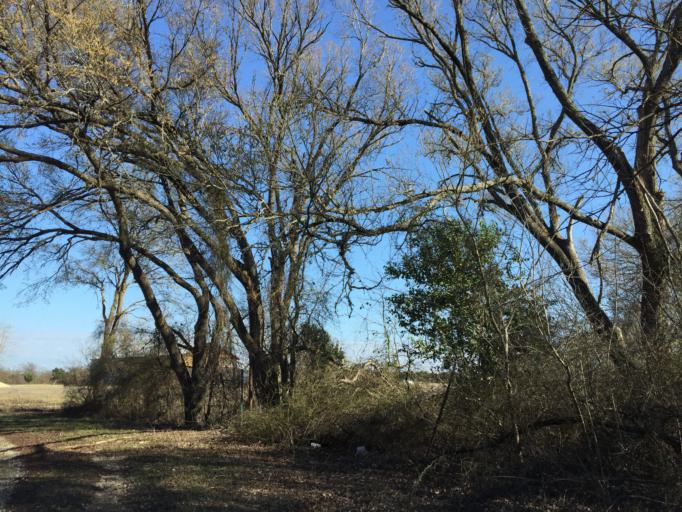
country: US
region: Texas
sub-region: Williamson County
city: Florence
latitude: 30.7715
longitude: -97.8372
